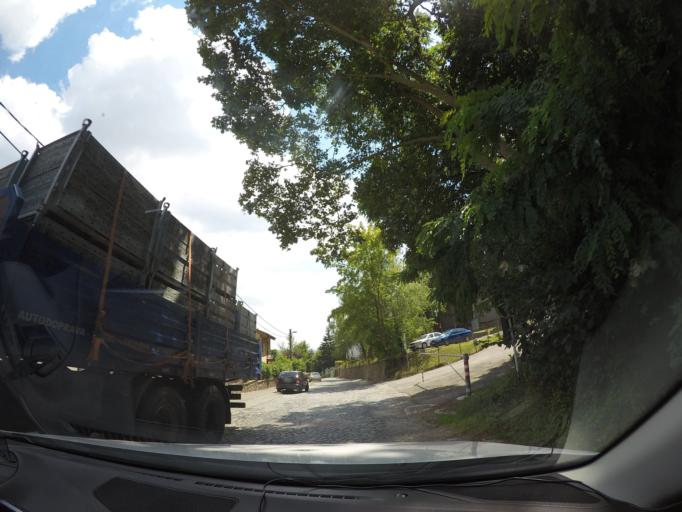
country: SK
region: Bratislavsky
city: Bratislava
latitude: 48.1771
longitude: 17.1127
